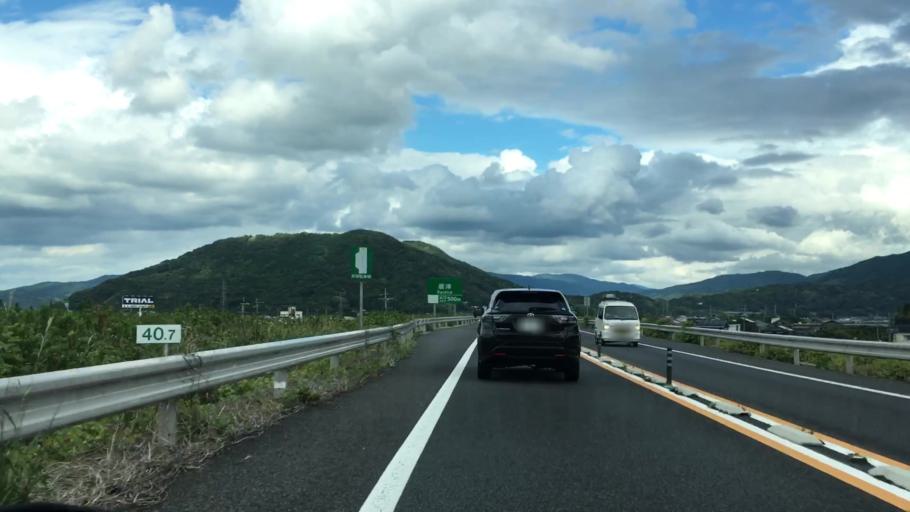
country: JP
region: Saga Prefecture
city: Karatsu
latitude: 33.4133
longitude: 129.9926
